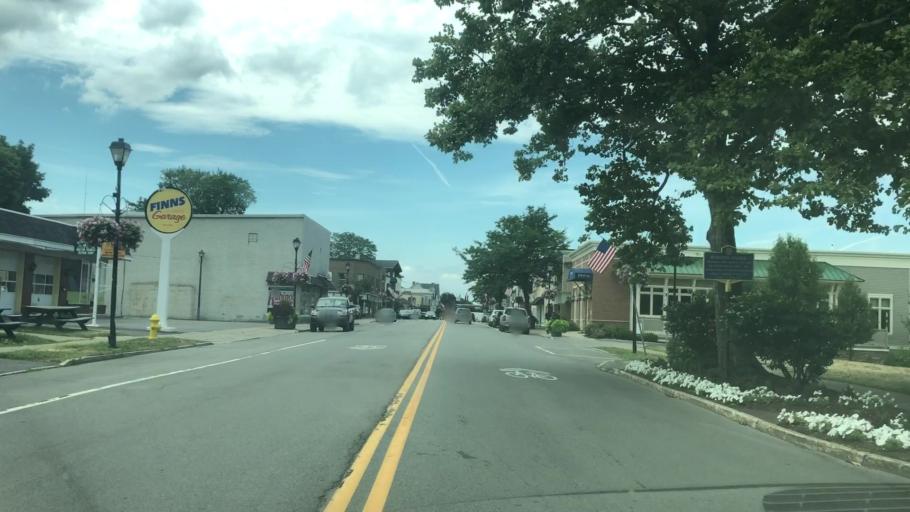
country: US
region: New York
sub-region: Monroe County
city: Webster
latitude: 43.2126
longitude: -77.4280
